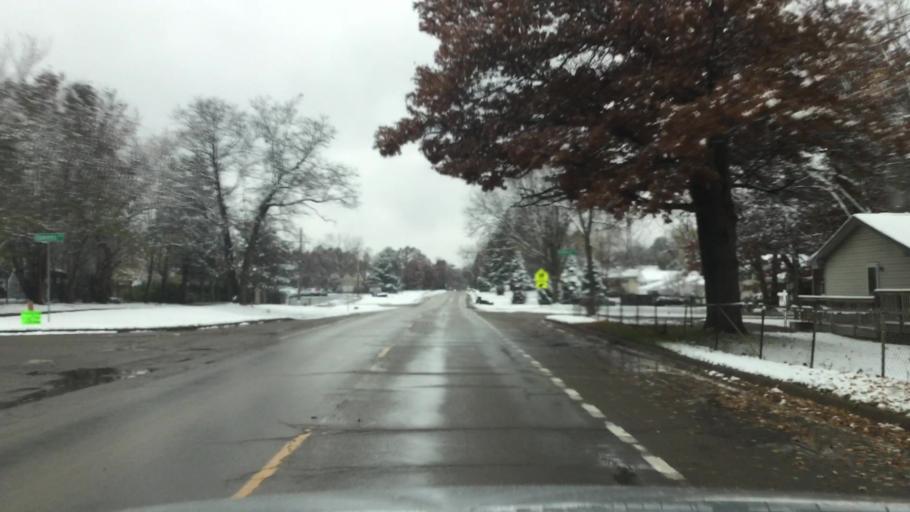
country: US
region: Michigan
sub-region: Oakland County
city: Oxford
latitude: 42.8091
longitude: -83.2971
